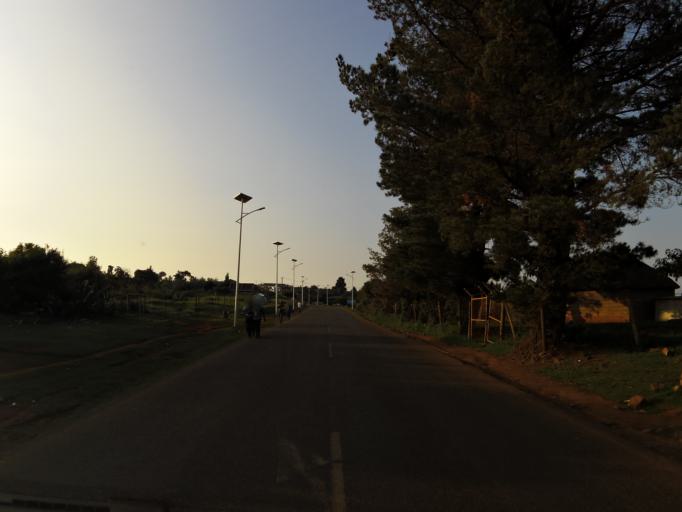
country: LS
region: Leribe
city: Leribe
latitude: -29.0058
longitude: 28.2125
